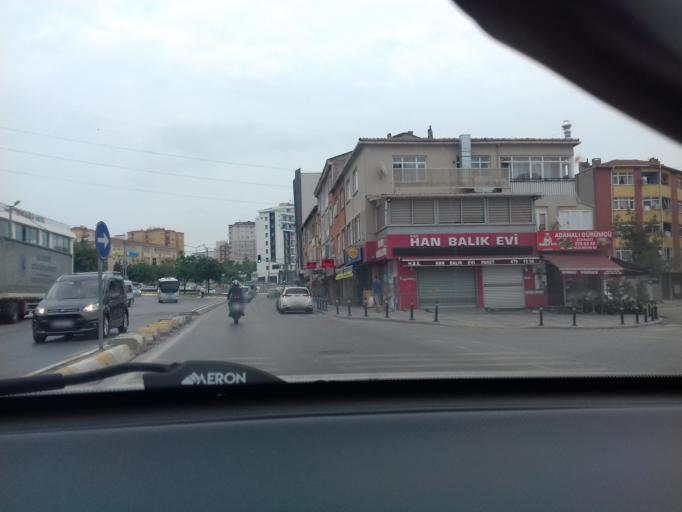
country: TR
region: Istanbul
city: Pendik
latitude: 40.9156
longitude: 29.3039
